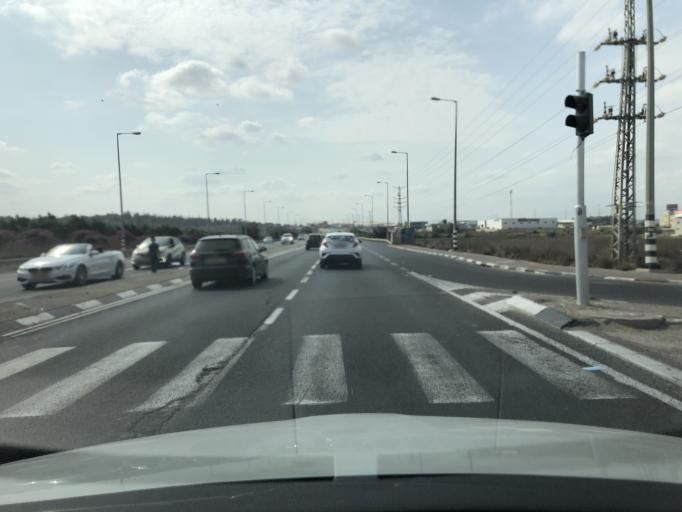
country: IL
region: Central District
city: Tirah
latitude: 32.2320
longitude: 34.9841
